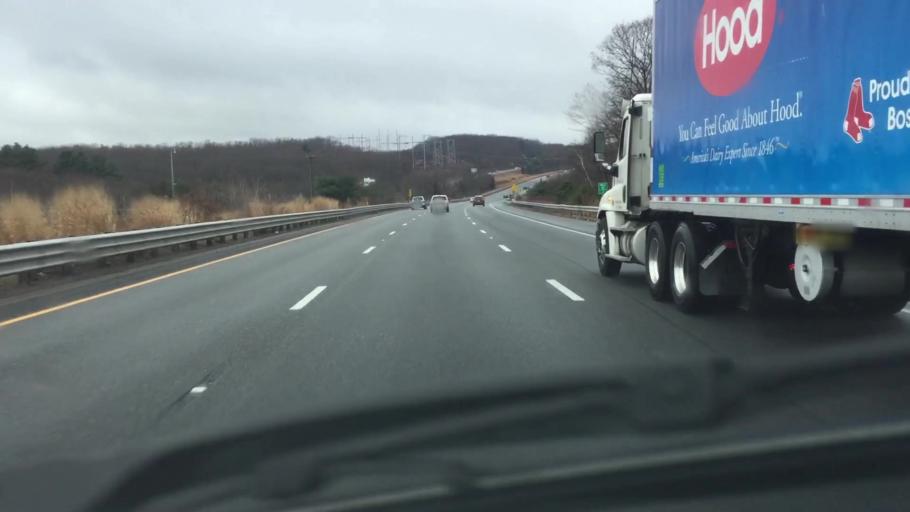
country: US
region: Massachusetts
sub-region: Worcester County
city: Milford
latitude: 42.1660
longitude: -71.5071
